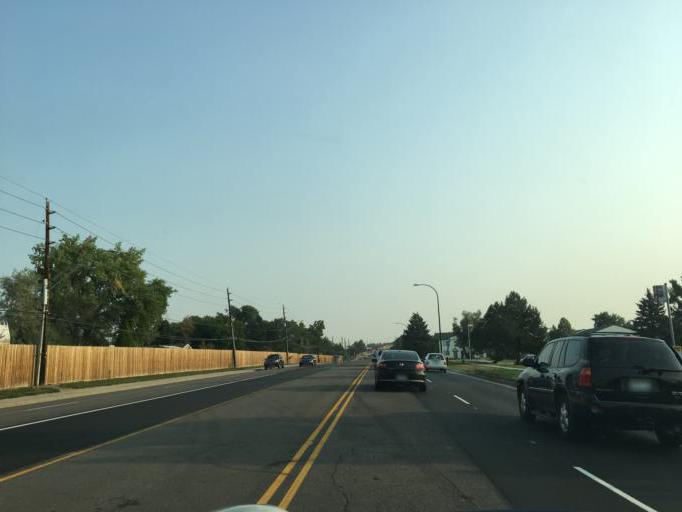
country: US
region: Colorado
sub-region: Adams County
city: Westminster
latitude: 39.8459
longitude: -105.0532
